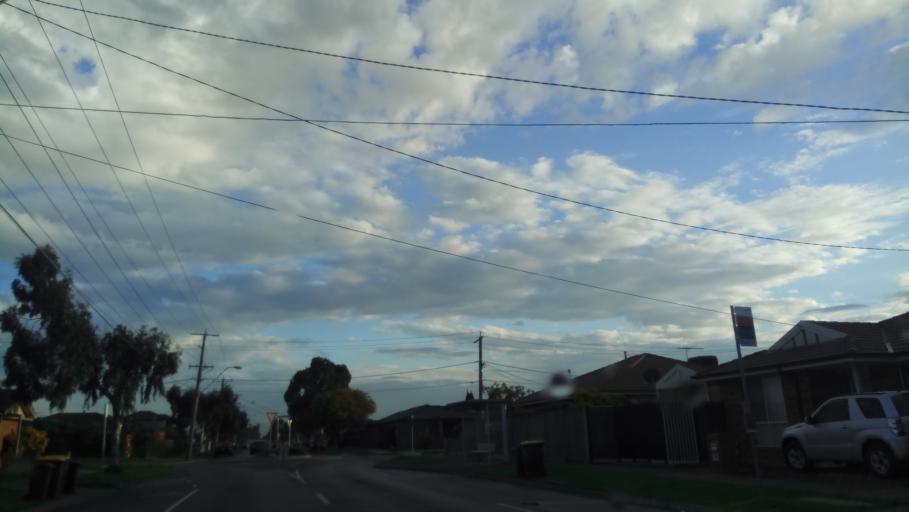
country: AU
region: Victoria
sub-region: Hobsons Bay
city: Altona Meadows
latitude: -37.8803
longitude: 144.7764
